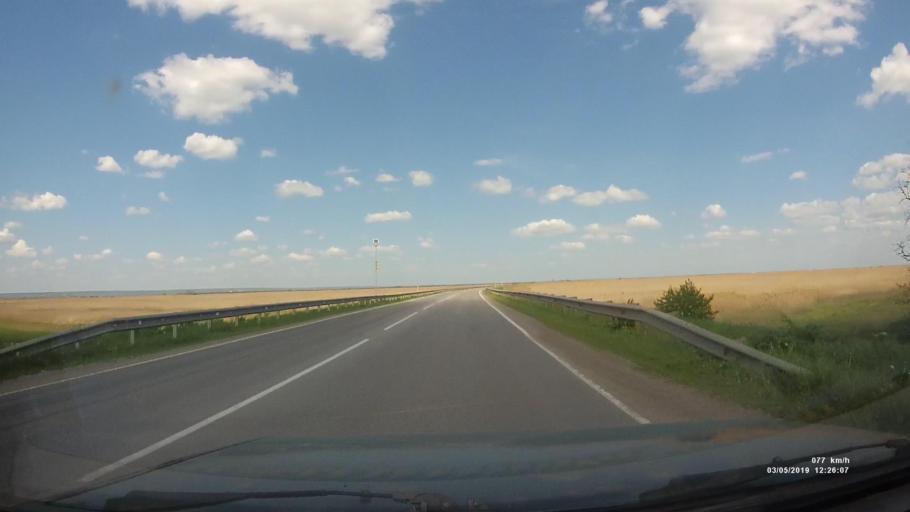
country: RU
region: Rostov
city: Semikarakorsk
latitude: 47.4410
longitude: 40.7121
